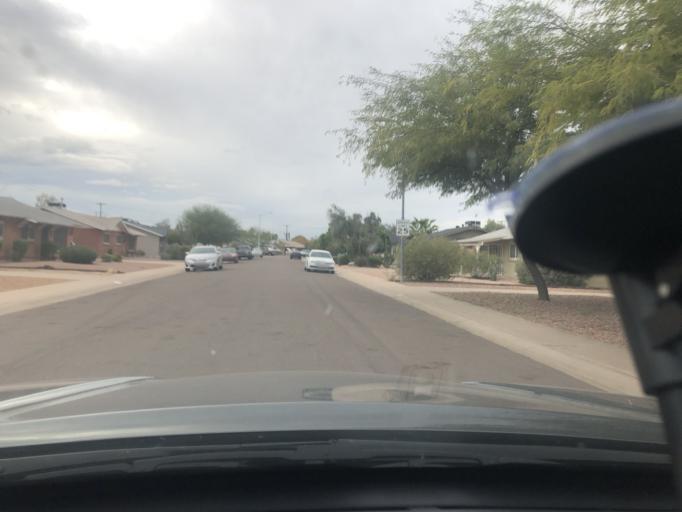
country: US
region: Arizona
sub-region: Maricopa County
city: Scottsdale
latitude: 33.4817
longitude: -111.8965
